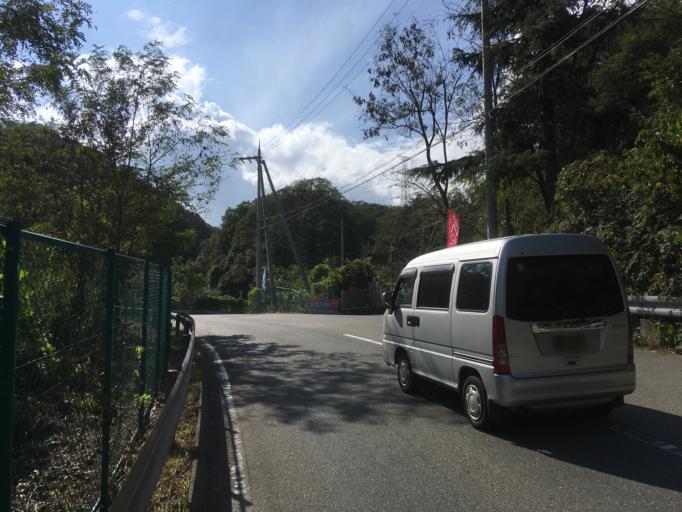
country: JP
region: Nara
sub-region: Ikoma-shi
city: Ikoma
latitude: 34.7360
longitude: 135.6807
